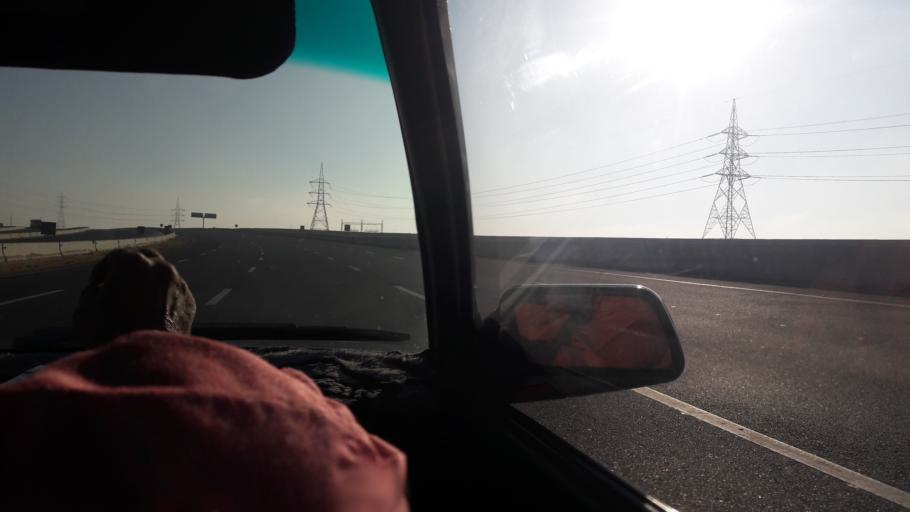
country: EG
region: Muhafazat al Qahirah
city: Halwan
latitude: 29.9212
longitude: 31.5211
